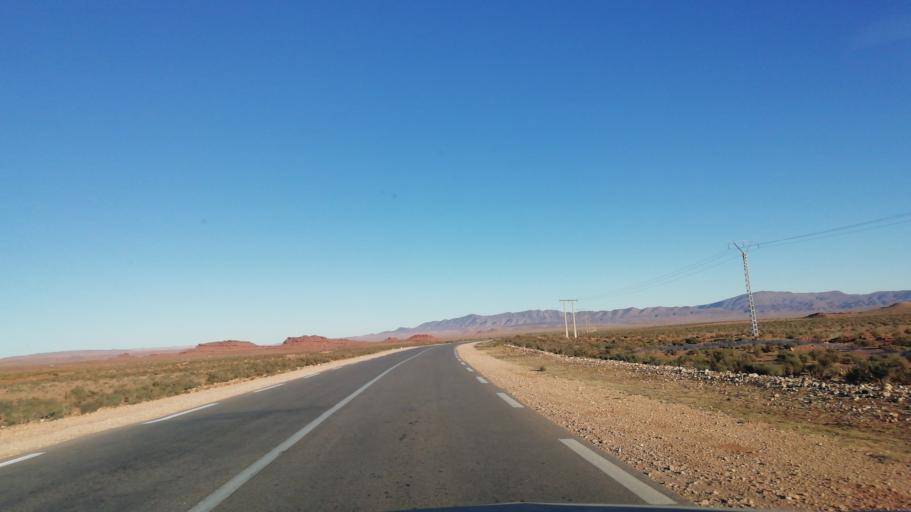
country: DZ
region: El Bayadh
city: El Abiodh Sidi Cheikh
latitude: 33.1704
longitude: 0.4899
